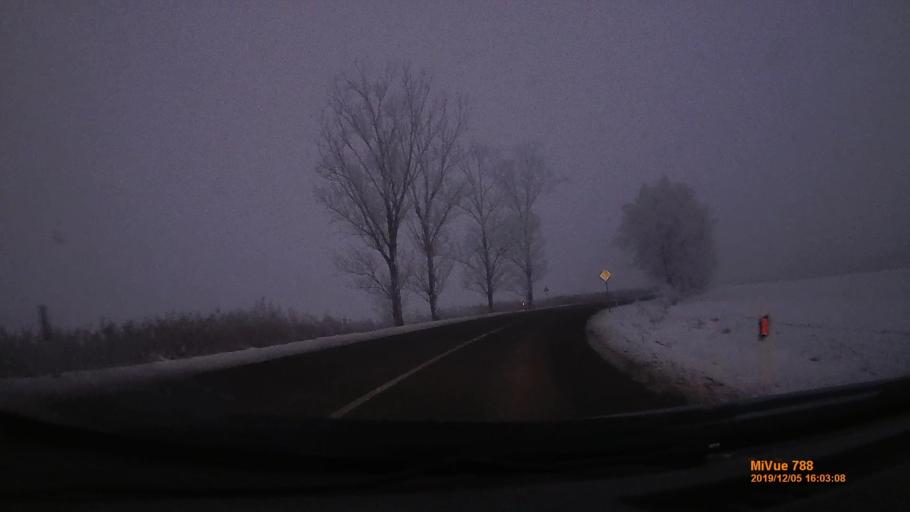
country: HU
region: Borsod-Abauj-Zemplen
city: Tarcal
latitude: 48.1011
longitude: 21.3724
